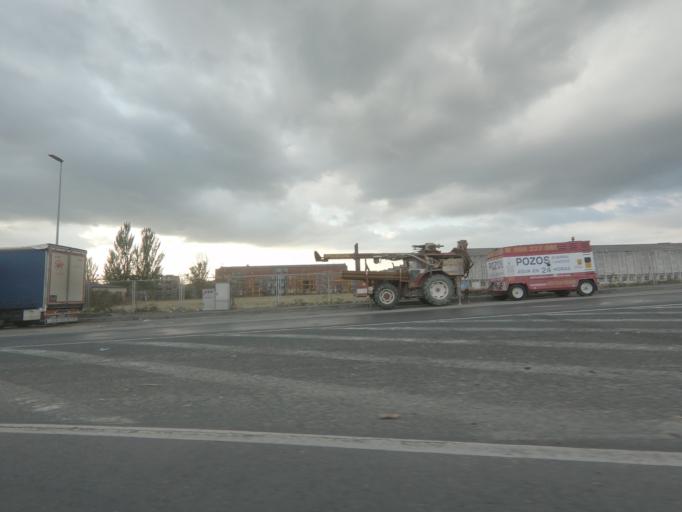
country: ES
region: Galicia
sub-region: Provincia de Ourense
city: Taboadela
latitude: 42.2900
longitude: -7.8164
